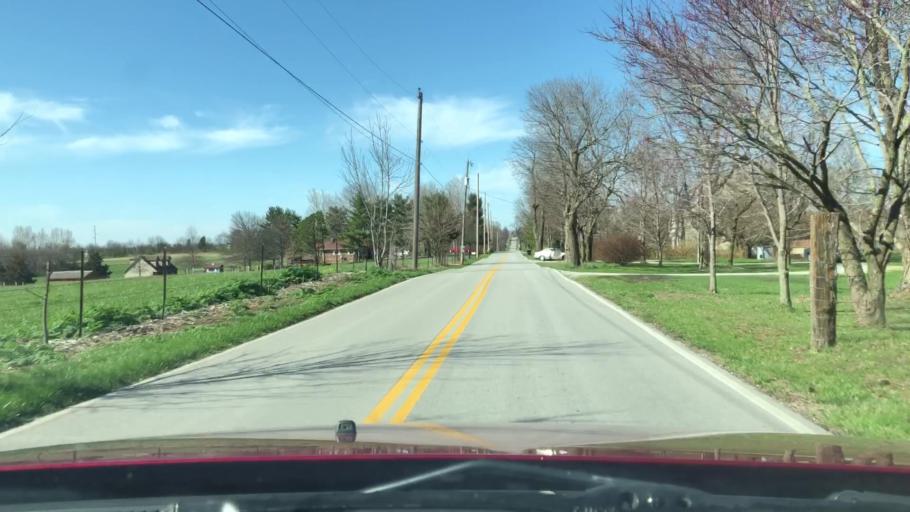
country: US
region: Missouri
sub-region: Greene County
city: Strafford
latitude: 37.2258
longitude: -93.1884
